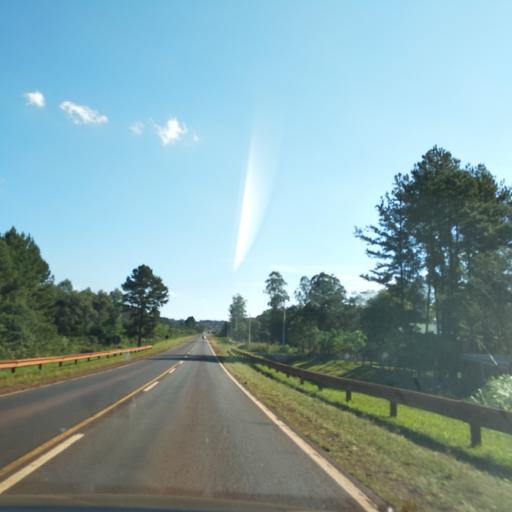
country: AR
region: Misiones
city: Jardin America
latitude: -27.0243
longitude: -55.2068
